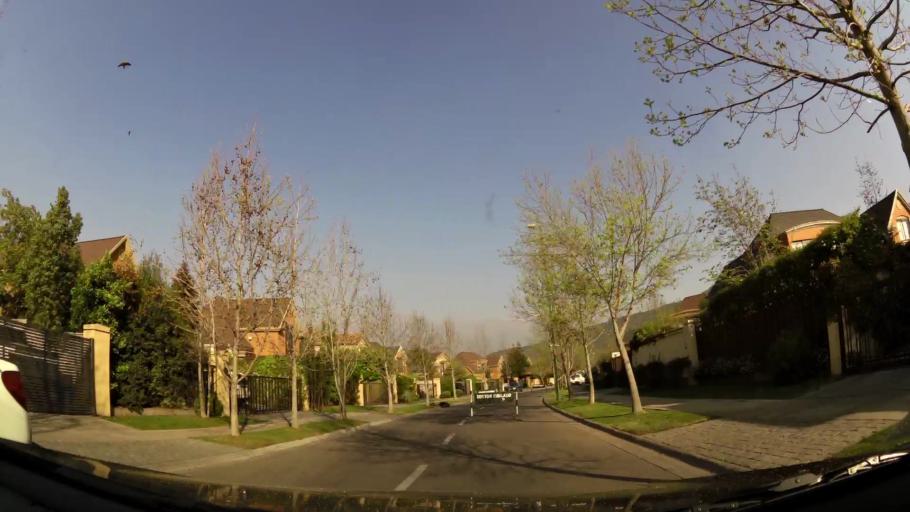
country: CL
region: Santiago Metropolitan
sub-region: Provincia de Santiago
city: Villa Presidente Frei, Nunoa, Santiago, Chile
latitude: -33.3586
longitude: -70.5354
